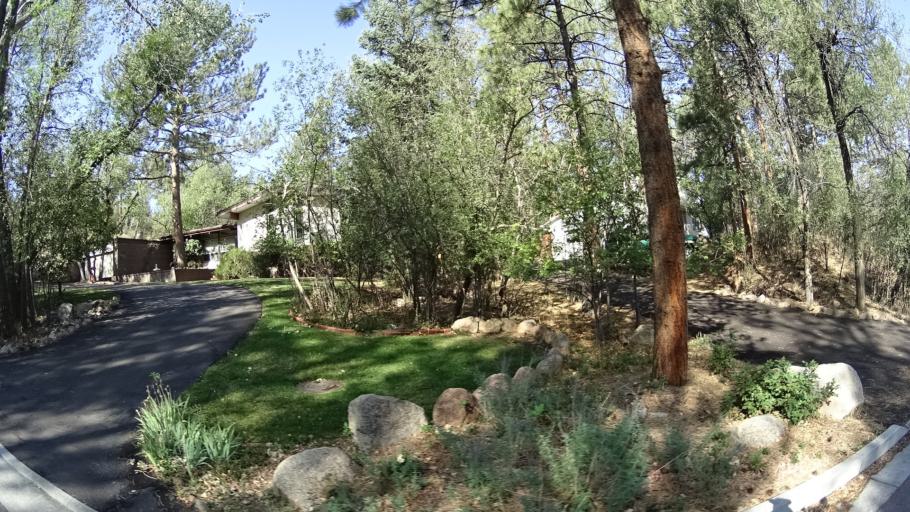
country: US
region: Colorado
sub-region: El Paso County
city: Colorado Springs
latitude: 38.7972
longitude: -104.8487
